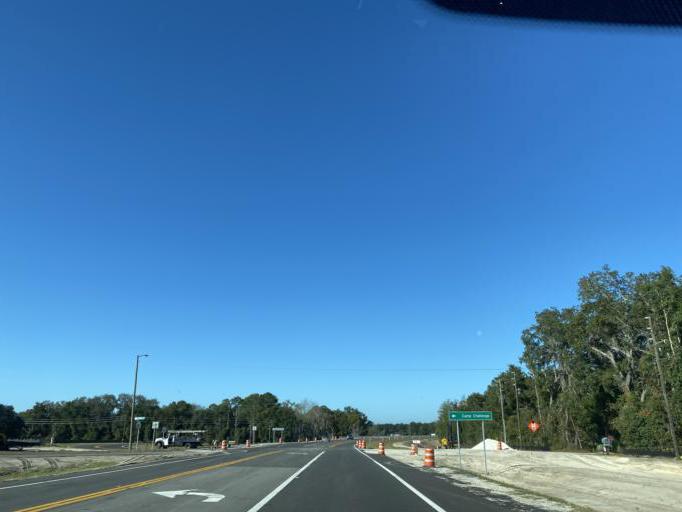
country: US
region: Florida
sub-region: Lake County
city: Mount Plymouth
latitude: 28.8126
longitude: -81.5147
